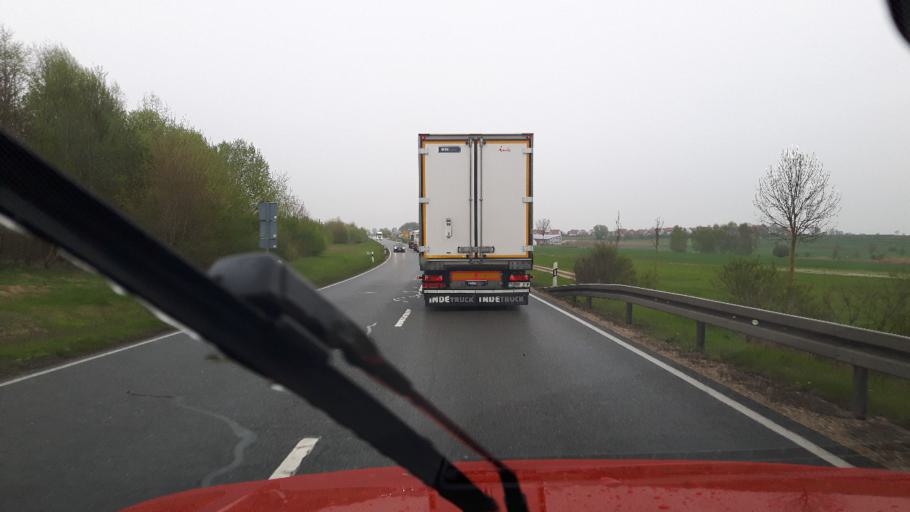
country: DE
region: Bavaria
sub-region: Regierungsbezirk Mittelfranken
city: Muhr am See
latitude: 49.1498
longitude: 10.7316
